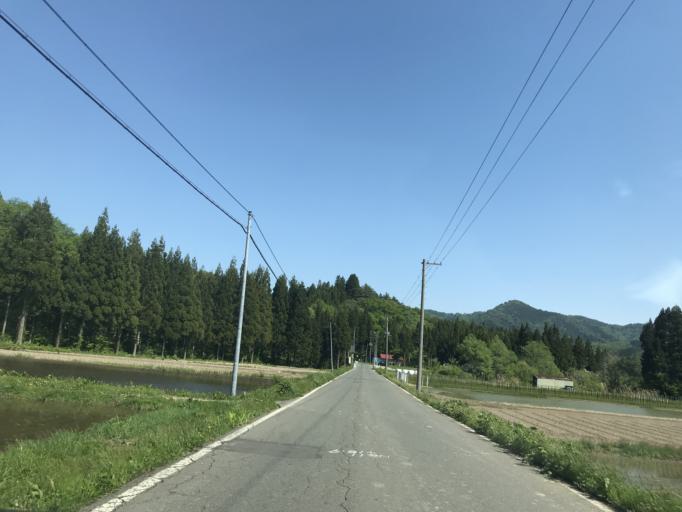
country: JP
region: Iwate
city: Shizukuishi
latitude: 39.5568
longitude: 140.8440
